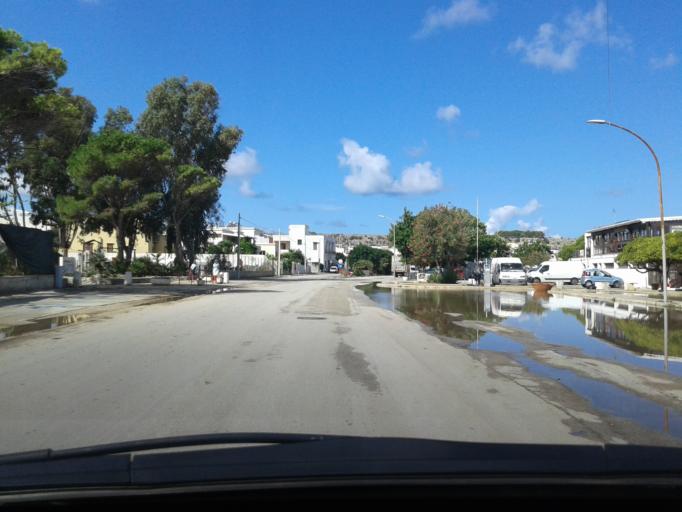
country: IT
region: Sicily
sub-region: Trapani
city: San Vito Lo Capo
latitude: 38.1746
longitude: 12.7415
